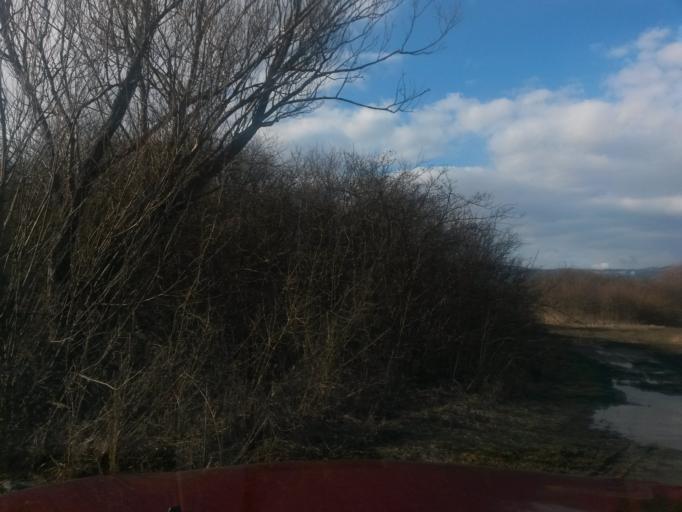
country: SK
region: Kosicky
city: Sobrance
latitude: 48.7767
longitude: 22.0881
